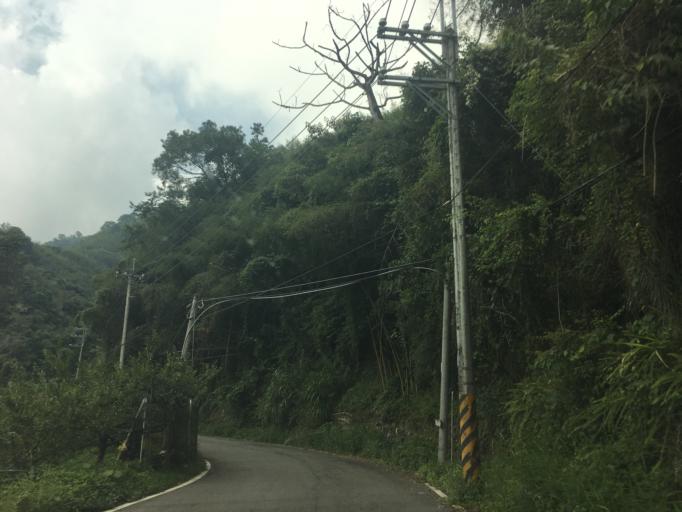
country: TW
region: Taiwan
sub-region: Miaoli
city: Miaoli
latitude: 24.3953
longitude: 120.9782
